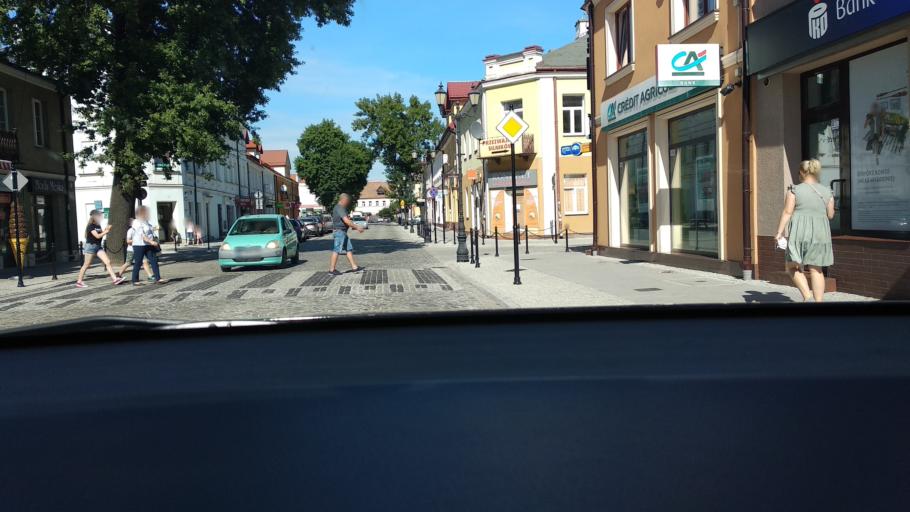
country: PL
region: Masovian Voivodeship
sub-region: Powiat pultuski
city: Pultusk
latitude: 52.7049
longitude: 21.0886
